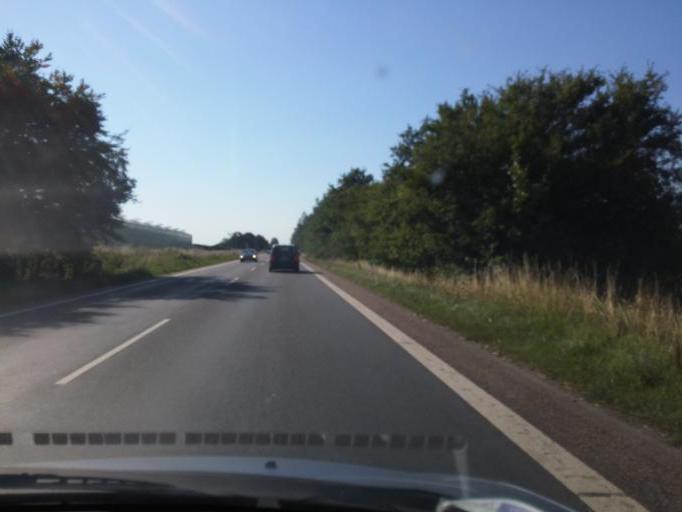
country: DK
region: South Denmark
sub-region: Odense Kommune
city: Bullerup
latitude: 55.3879
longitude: 10.4922
